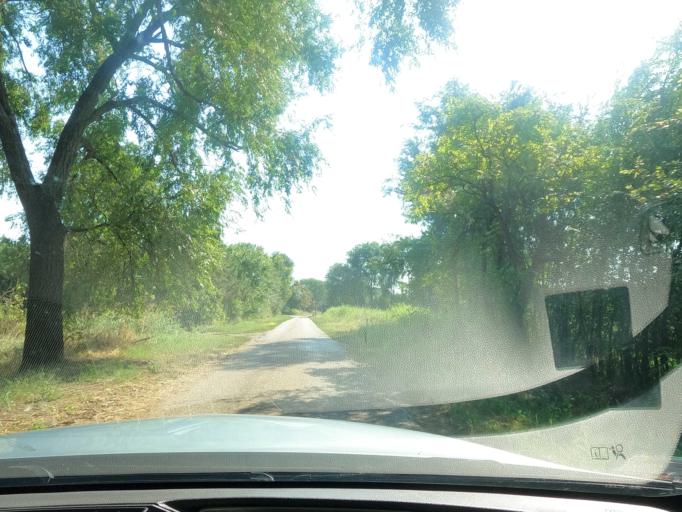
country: RS
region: Autonomna Pokrajina Vojvodina
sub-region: Juznobacki Okrug
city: Becej
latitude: 45.6563
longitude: 19.9006
